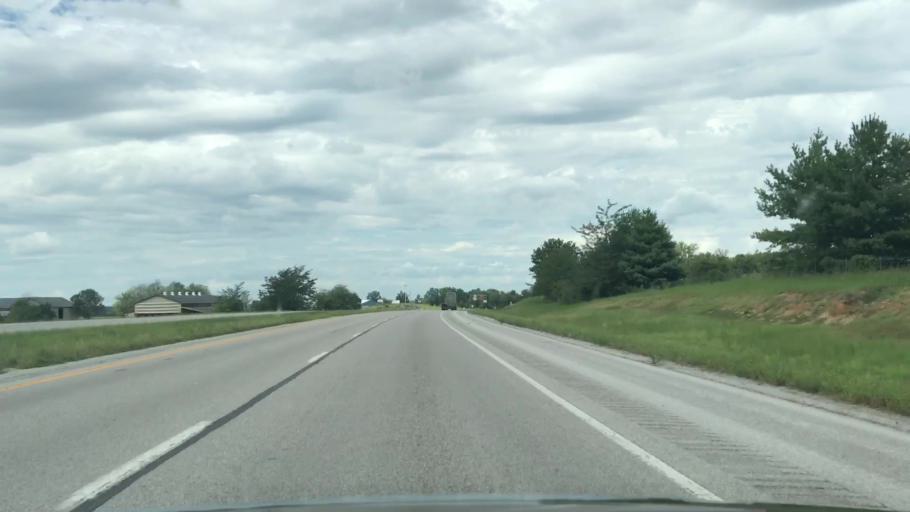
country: US
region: Kentucky
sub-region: Todd County
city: Elkton
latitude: 36.8262
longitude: -87.2167
